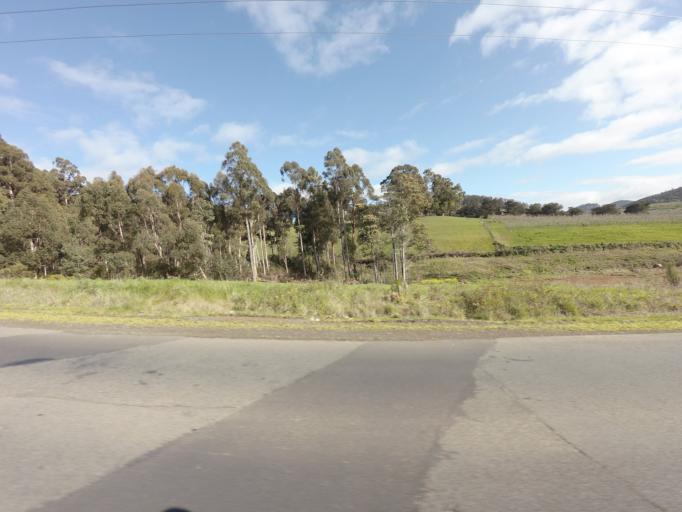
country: AU
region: Tasmania
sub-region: Huon Valley
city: Geeveston
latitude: -43.1936
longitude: 146.9577
